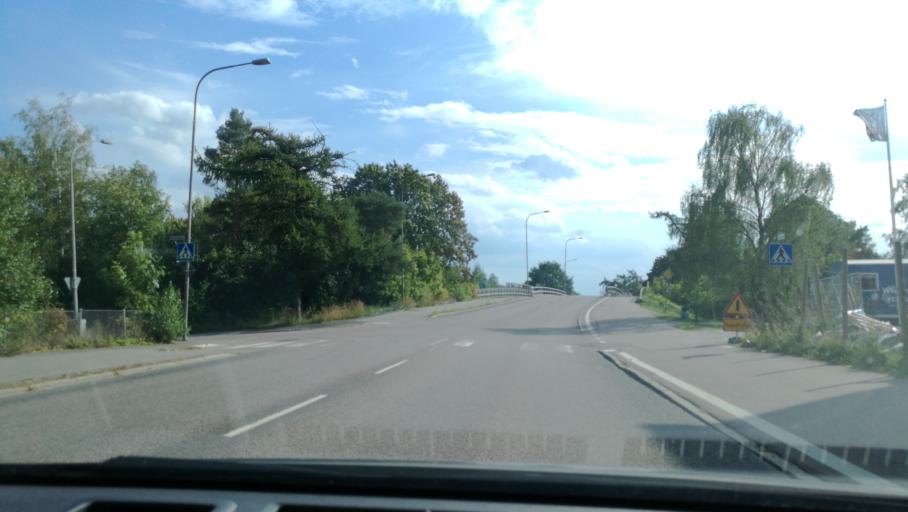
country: SE
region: Vaestmanland
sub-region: Vasteras
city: Vasteras
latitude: 59.5987
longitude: 16.5236
